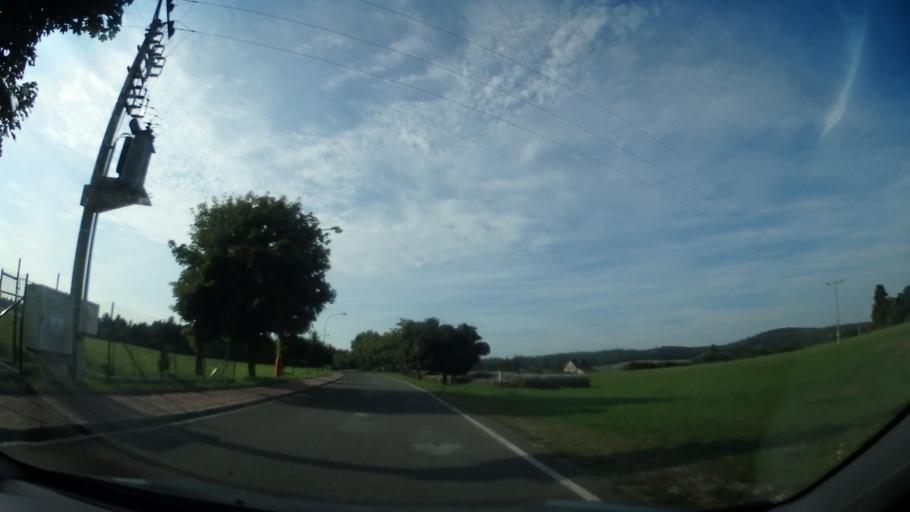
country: CZ
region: Jihocesky
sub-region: Okres Pisek
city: Pisek
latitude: 49.3879
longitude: 14.1275
